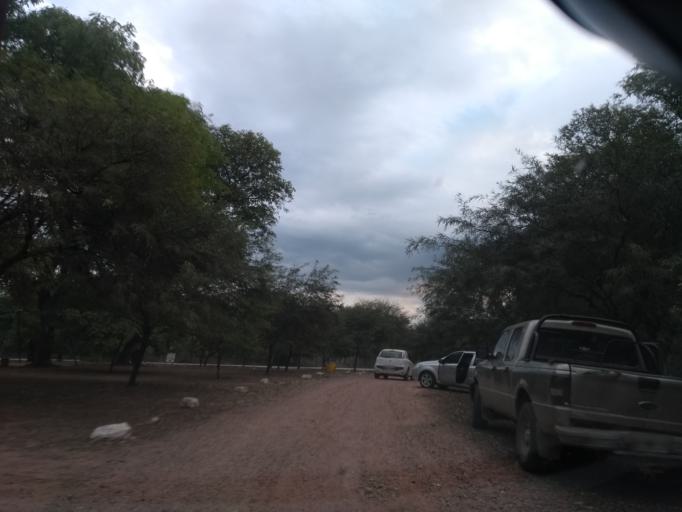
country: AR
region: Chaco
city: Presidencia Roque Saenz Pena
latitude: -26.8216
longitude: -60.4194
